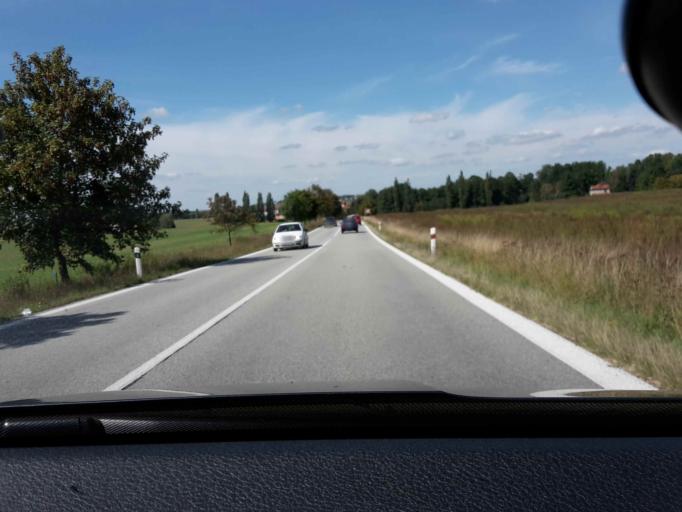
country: CZ
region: Jihocesky
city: Kardasova Recice
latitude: 49.1770
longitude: 14.8672
